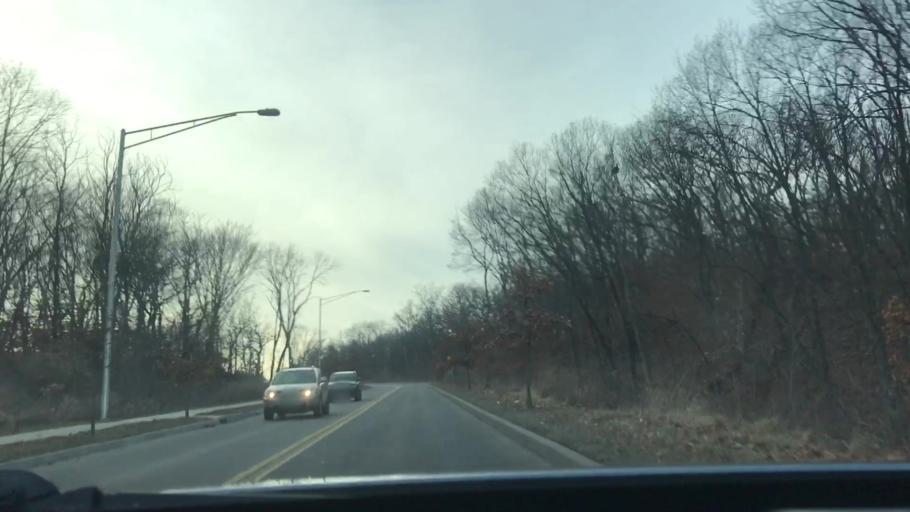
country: US
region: Missouri
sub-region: Platte County
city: Riverside
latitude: 39.2254
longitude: -94.6305
